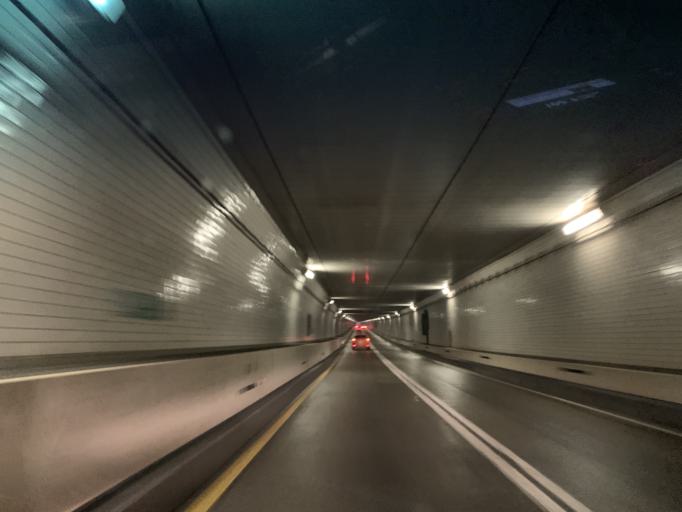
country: US
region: Maryland
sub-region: Baltimore County
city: Dundalk
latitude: 39.2573
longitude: -76.5692
